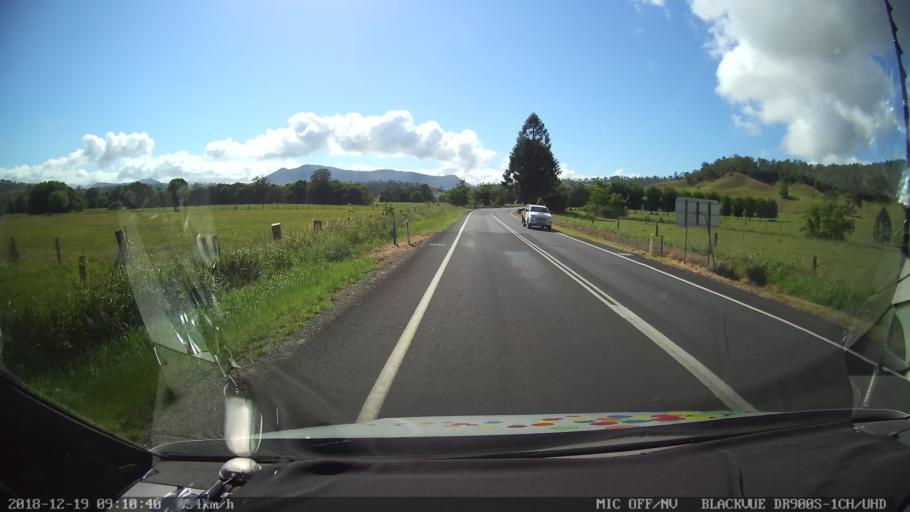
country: AU
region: New South Wales
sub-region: Kyogle
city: Kyogle
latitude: -28.4872
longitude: 152.9314
